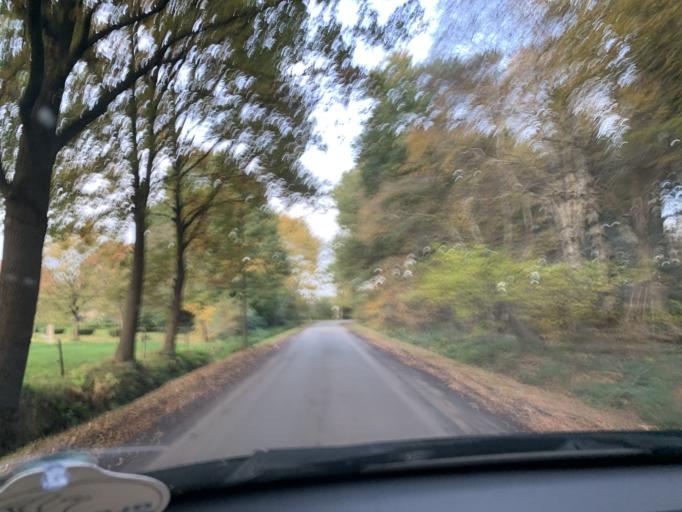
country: DE
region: Lower Saxony
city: Wiefelstede
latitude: 53.2505
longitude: 8.0682
